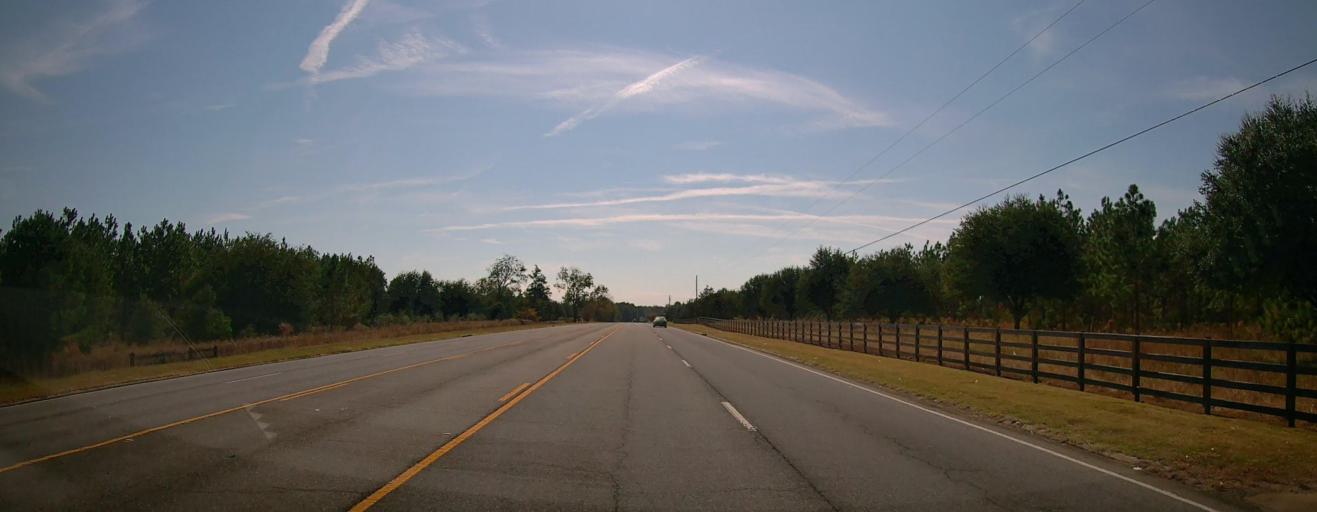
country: US
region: Georgia
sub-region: Lee County
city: Leesburg
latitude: 31.7682
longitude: -83.9725
